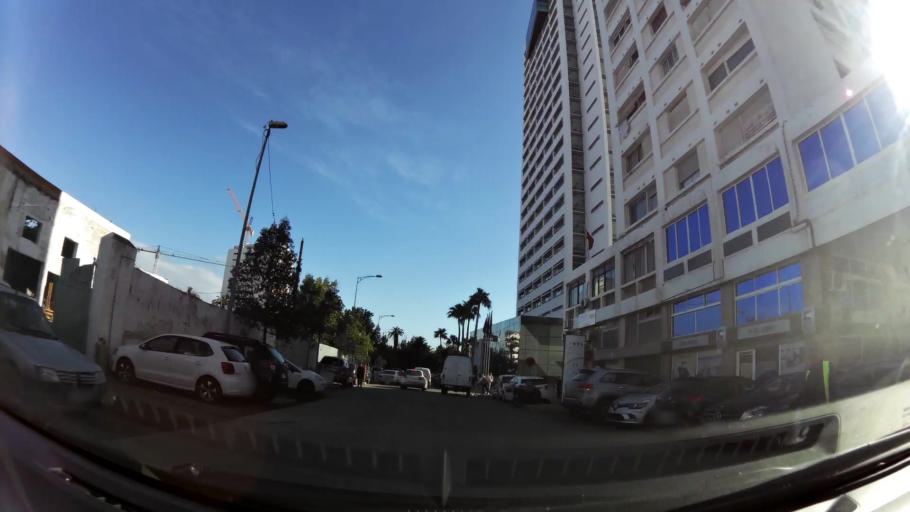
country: MA
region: Grand Casablanca
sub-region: Casablanca
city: Casablanca
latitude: 33.5976
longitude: -7.6144
